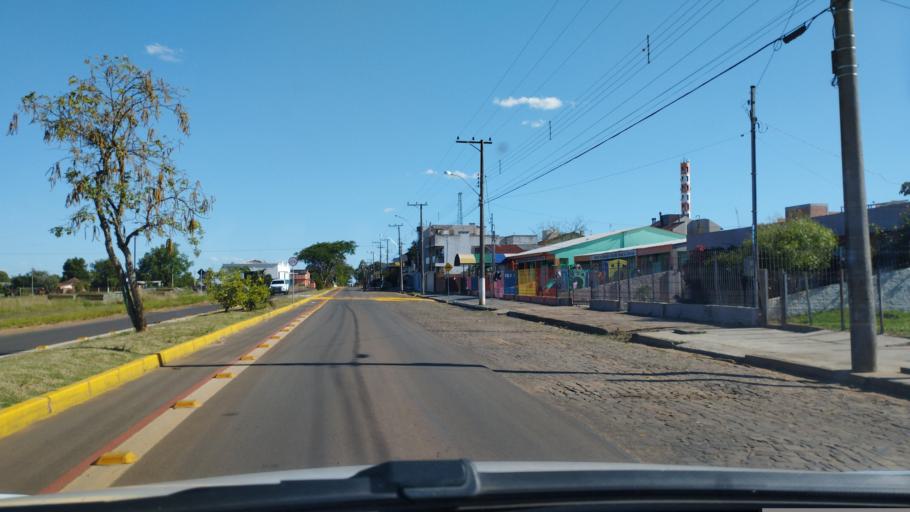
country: BR
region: Rio Grande do Sul
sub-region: Tupancireta
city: Tupancireta
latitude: -29.0782
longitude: -53.8362
